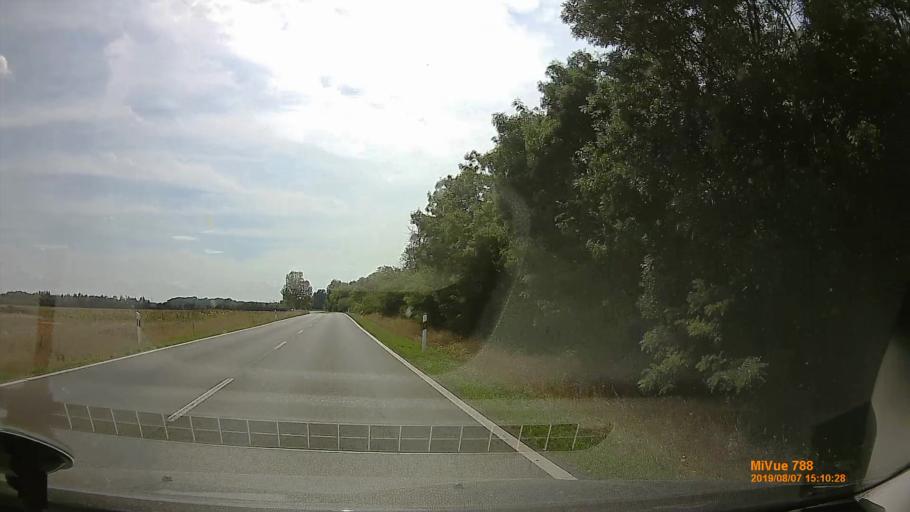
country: HU
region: Vas
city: Repcelak
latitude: 47.4040
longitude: 16.9921
